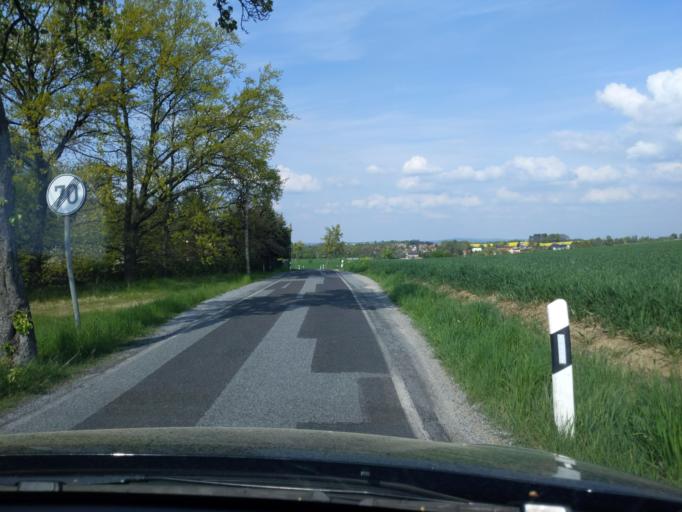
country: DE
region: Saxony
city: Kubschutz
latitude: 51.1648
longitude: 14.4743
